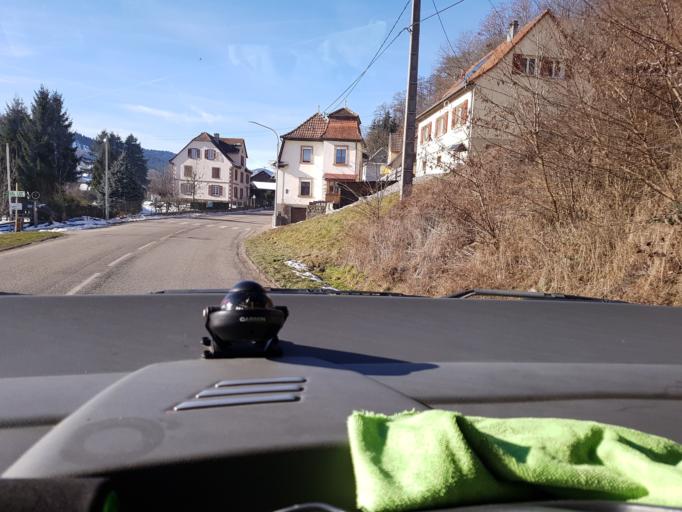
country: FR
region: Alsace
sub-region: Departement du Haut-Rhin
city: Stosswihr
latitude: 48.0283
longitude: 7.1032
